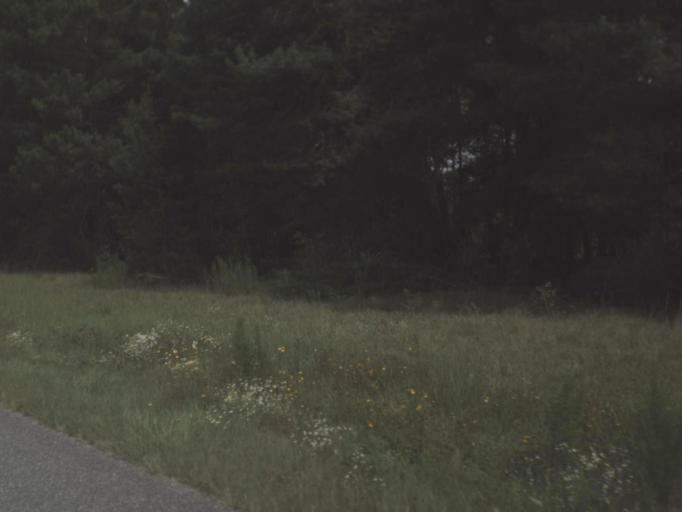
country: US
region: Florida
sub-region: Madison County
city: Madison
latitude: 30.4060
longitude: -83.2435
